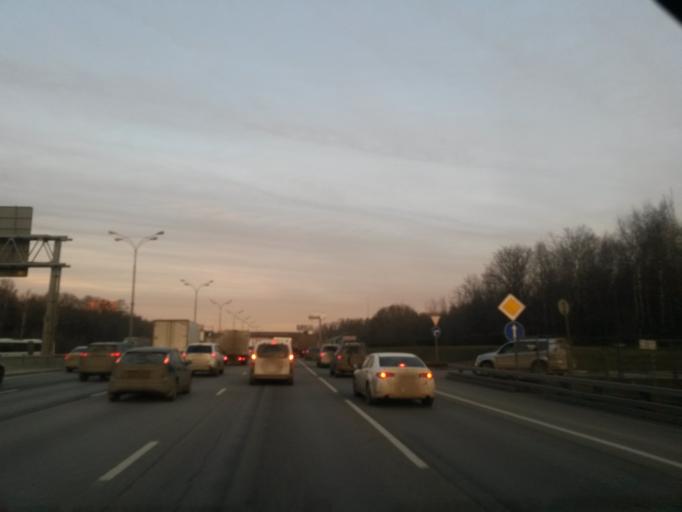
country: RU
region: Moscow
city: Tyoply Stan
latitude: 55.6189
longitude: 37.4833
